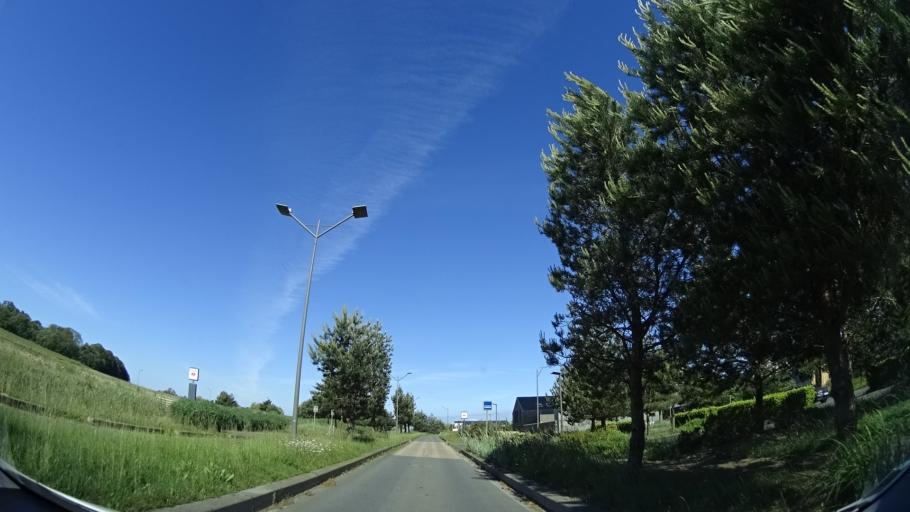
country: FR
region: Brittany
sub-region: Departement d'Ille-et-Vilaine
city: Saint-Jouan-des-Guerets
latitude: 48.6128
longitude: -1.9744
